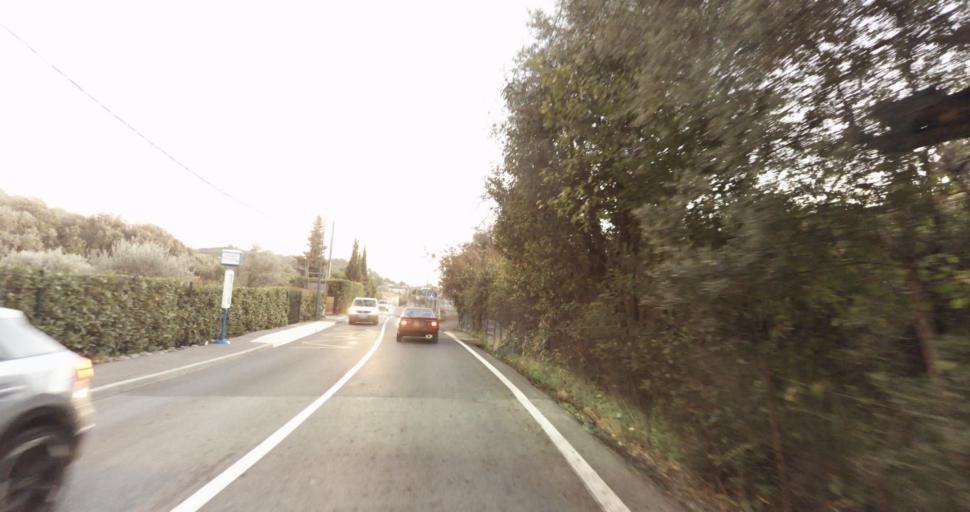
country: FR
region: Provence-Alpes-Cote d'Azur
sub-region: Departement des Alpes-Maritimes
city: Saint-Paul-de-Vence
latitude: 43.7112
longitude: 7.1297
